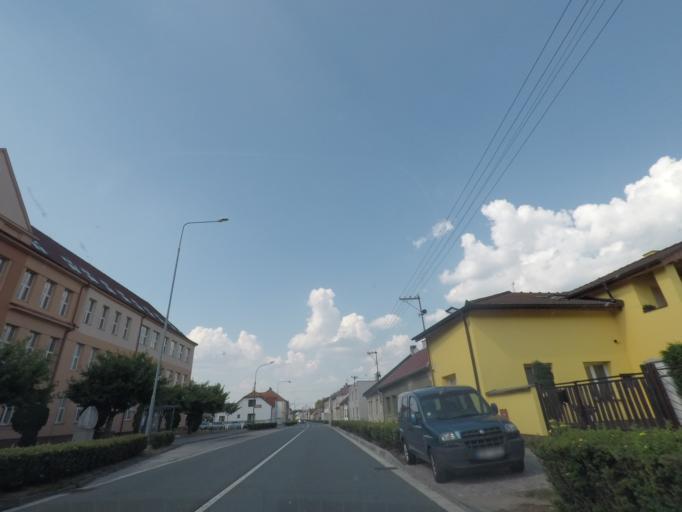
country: CZ
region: Pardubicky
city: Horni Jeleni
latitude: 50.0454
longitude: 16.0828
